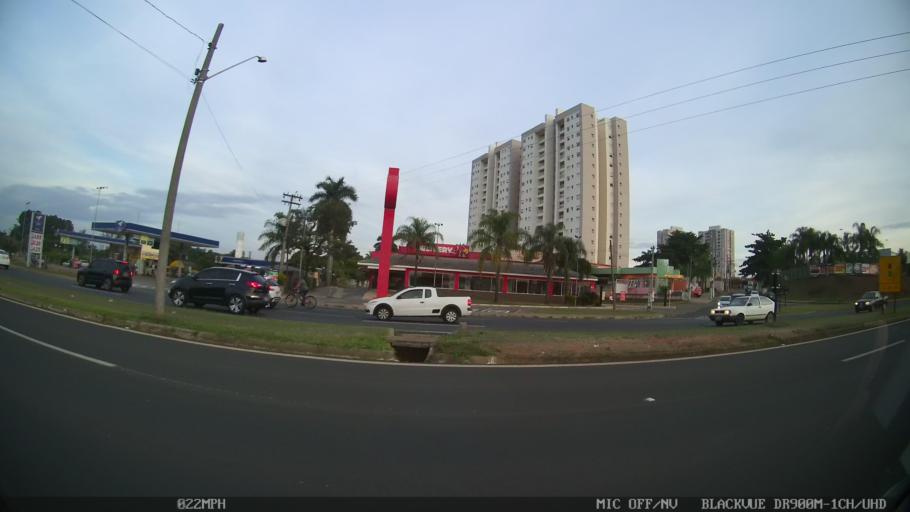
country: BR
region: Sao Paulo
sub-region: Limeira
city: Limeira
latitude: -22.5621
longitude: -47.4193
